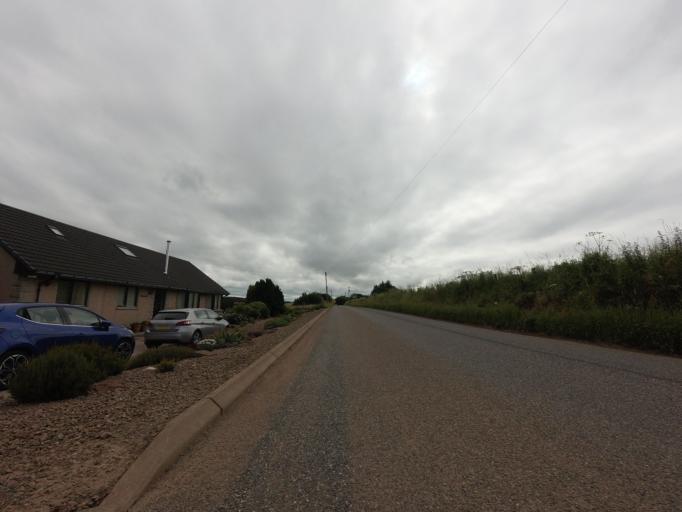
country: GB
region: Scotland
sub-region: Aberdeenshire
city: Turriff
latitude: 57.5408
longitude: -2.3673
